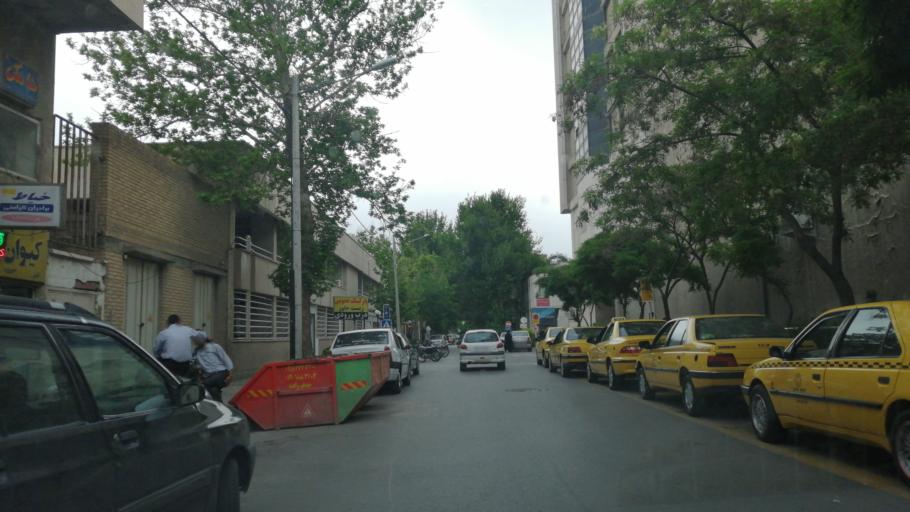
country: IR
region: Razavi Khorasan
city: Mashhad
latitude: 36.2904
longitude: 59.5851
